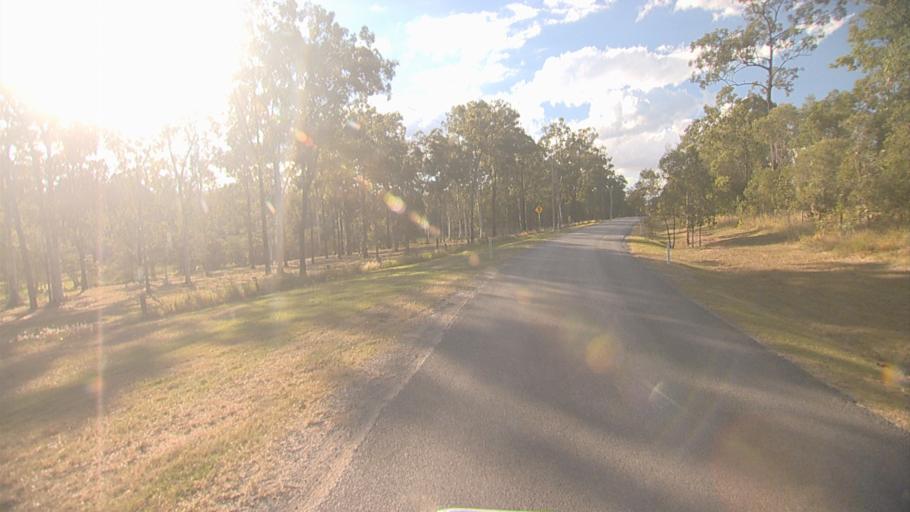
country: AU
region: Queensland
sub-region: Logan
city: North Maclean
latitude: -27.7471
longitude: 152.9407
